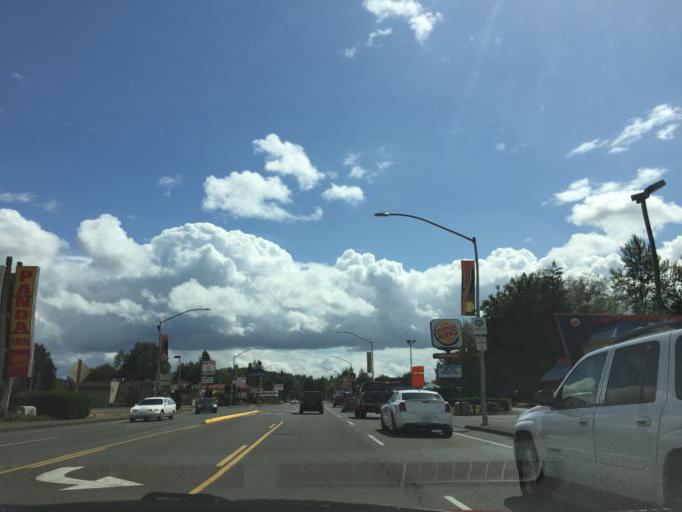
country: US
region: Washington
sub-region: Lewis County
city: Fords Prairie
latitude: 46.7253
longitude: -122.9736
